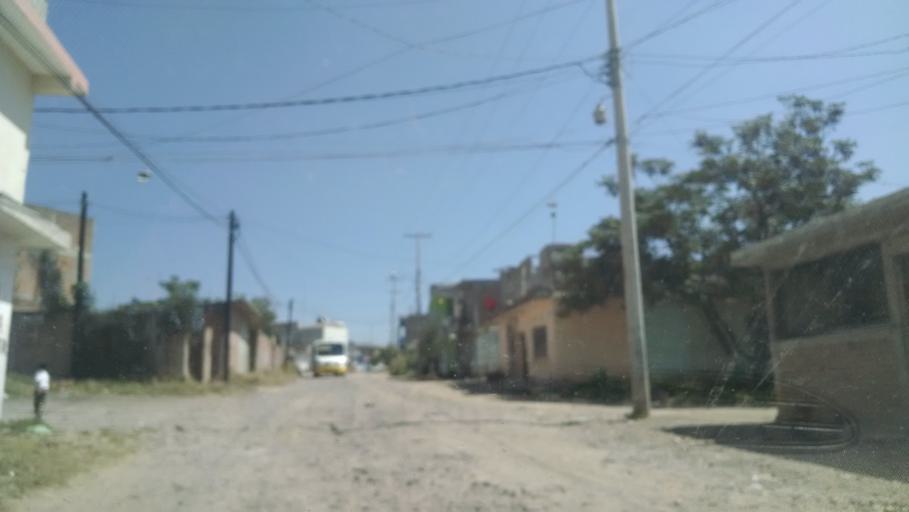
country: MX
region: Guanajuato
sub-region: Leon
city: La Ermita
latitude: 21.1497
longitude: -101.7355
